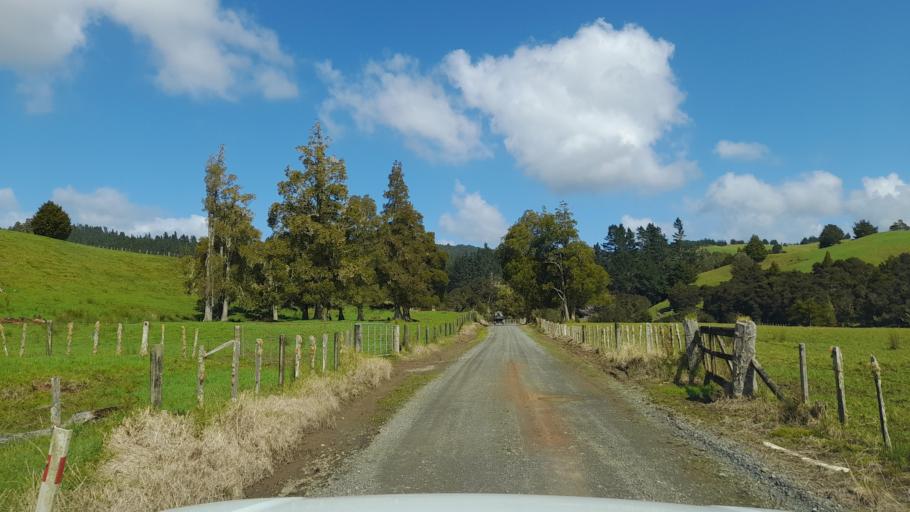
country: NZ
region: Northland
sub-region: Far North District
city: Waimate North
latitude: -35.1555
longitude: 173.7145
